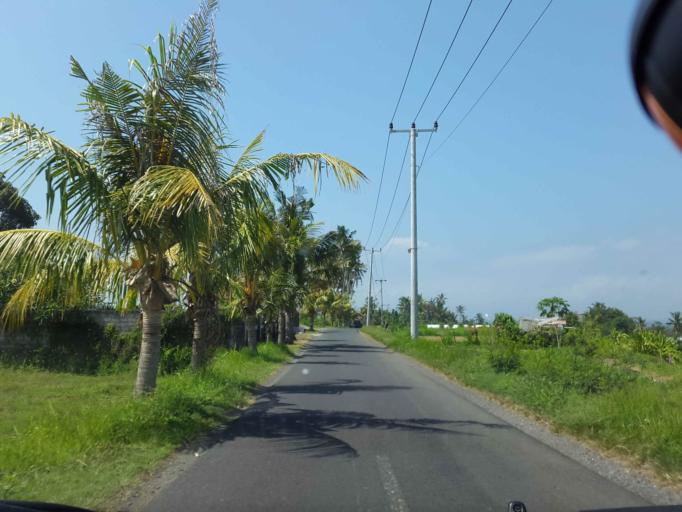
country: ID
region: Bali
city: Klungkung
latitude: -8.5623
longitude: 115.3723
